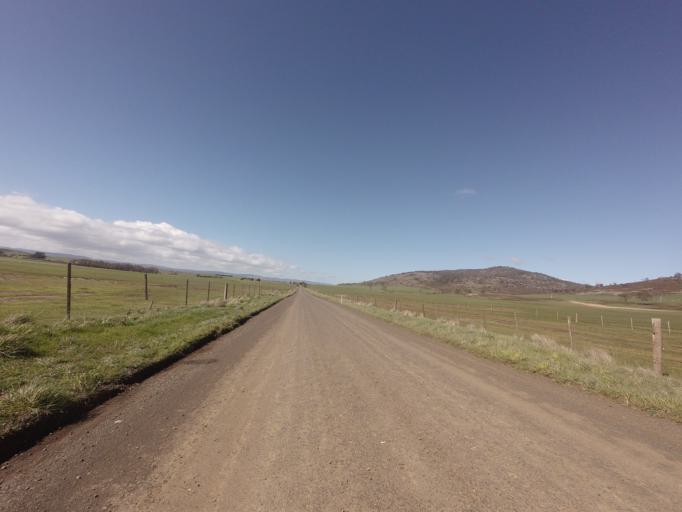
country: AU
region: Tasmania
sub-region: Northern Midlands
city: Evandale
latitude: -41.9127
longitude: 147.3775
